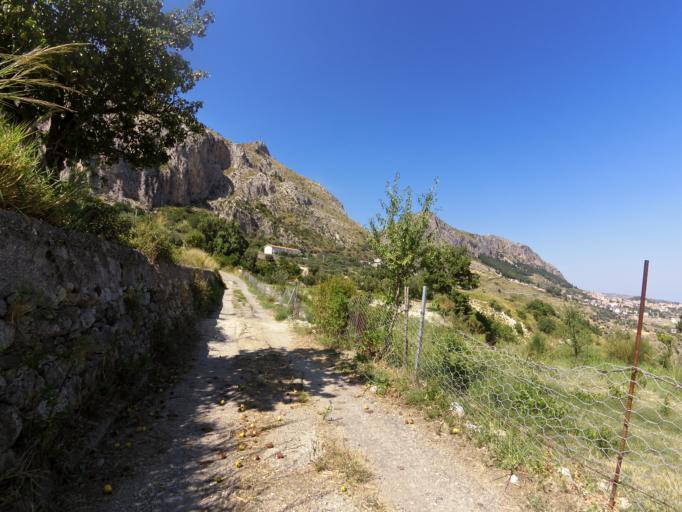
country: IT
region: Calabria
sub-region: Provincia di Reggio Calabria
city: Pazzano
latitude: 38.4641
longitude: 16.4544
